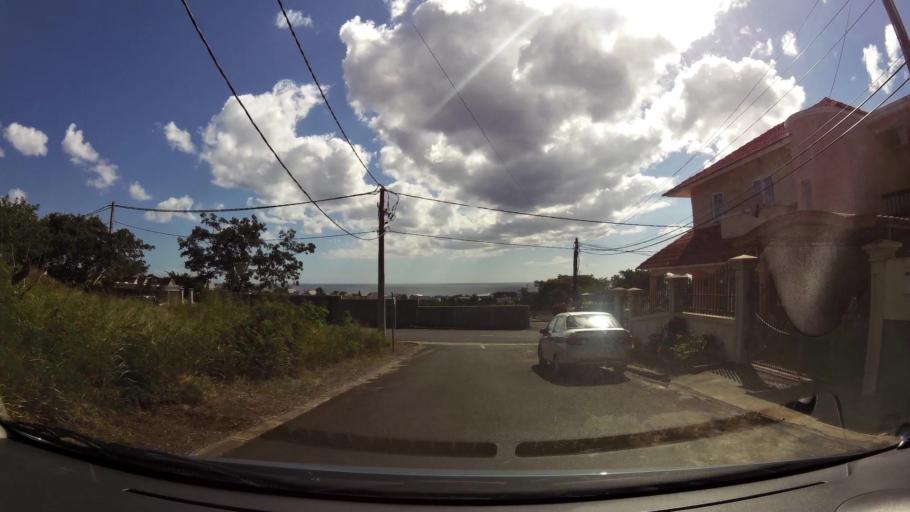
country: MU
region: Black River
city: Albion
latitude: -20.2212
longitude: 57.4165
